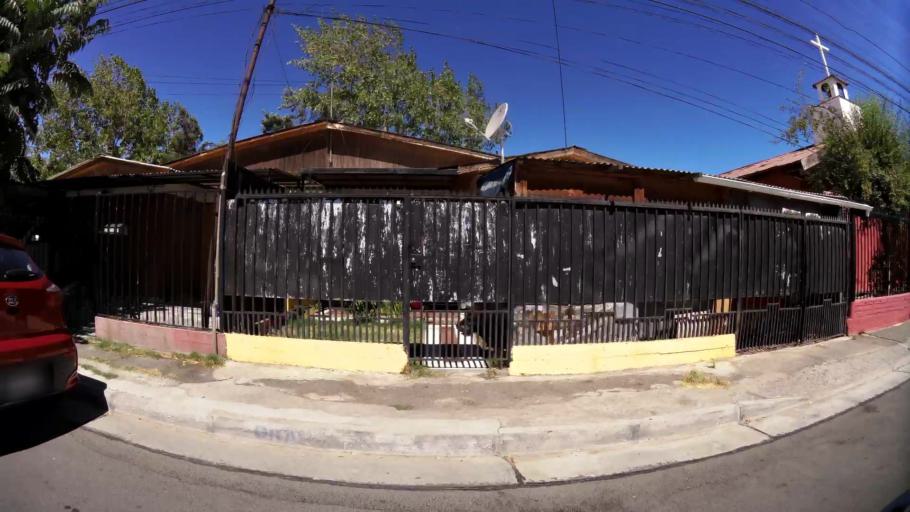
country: CL
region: O'Higgins
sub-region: Provincia de Cachapoal
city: Rancagua
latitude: -34.1709
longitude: -70.7649
